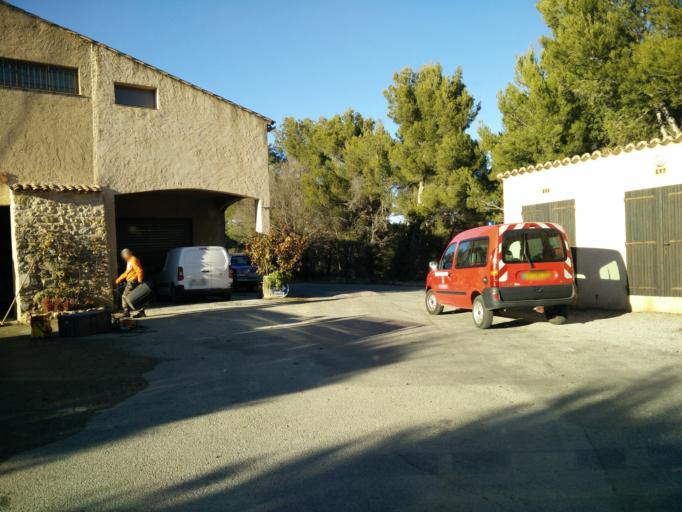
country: FR
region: Provence-Alpes-Cote d'Azur
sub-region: Departement du Var
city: Villecroze
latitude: 43.5878
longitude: 6.3060
